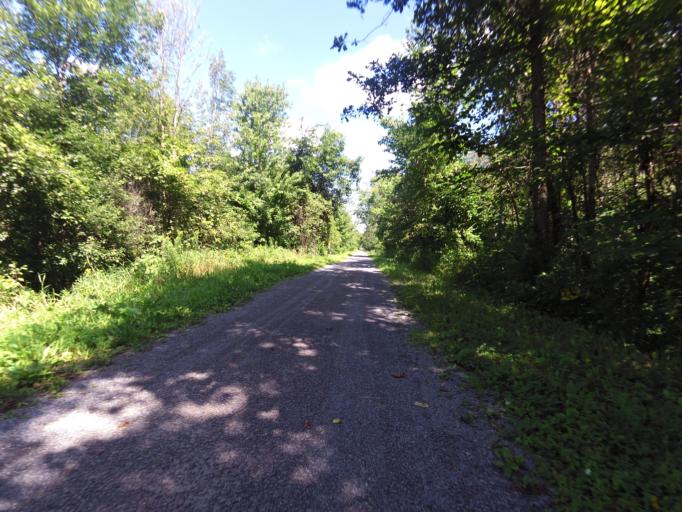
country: CA
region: Ontario
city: Ottawa
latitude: 45.2462
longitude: -75.6206
